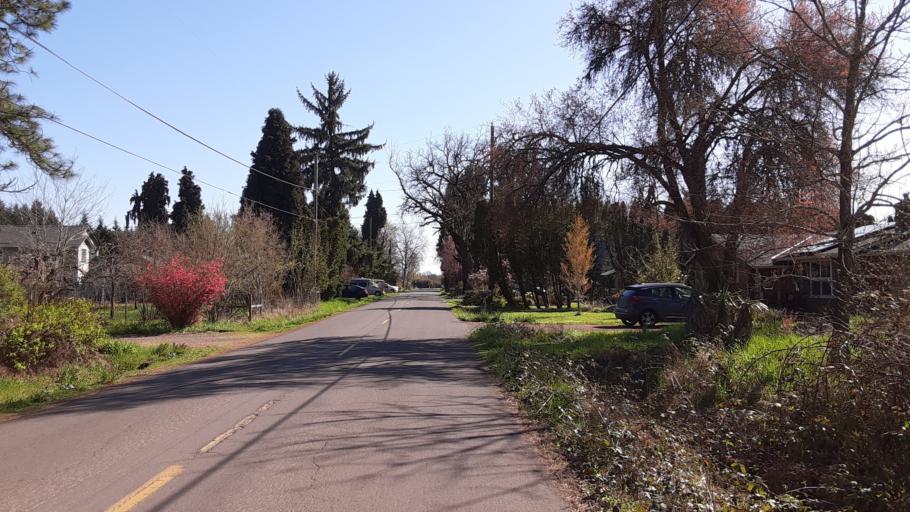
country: US
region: Oregon
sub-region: Benton County
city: Corvallis
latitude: 44.5412
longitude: -123.2558
